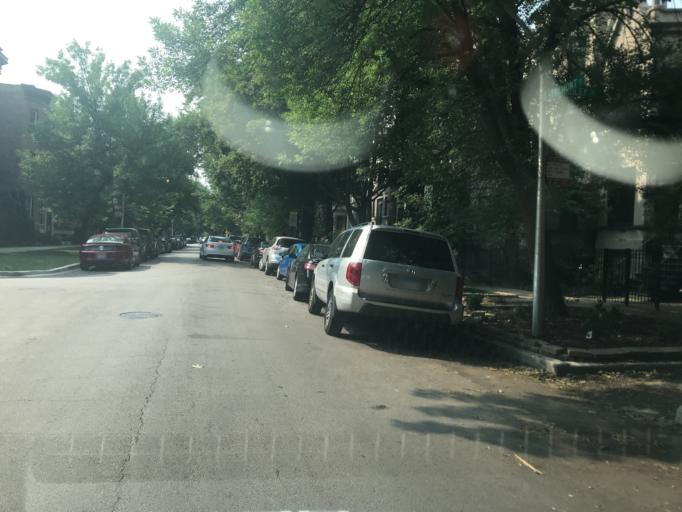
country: US
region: Illinois
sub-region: Cook County
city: Lincolnwood
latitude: 41.9503
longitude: -87.6520
